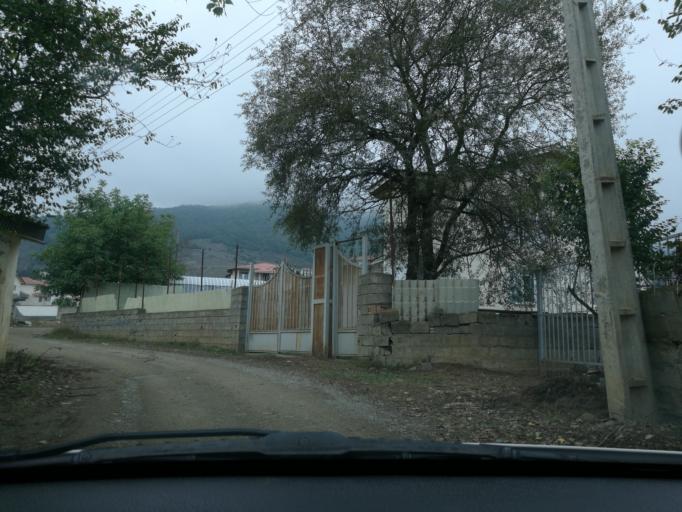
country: IR
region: Mazandaran
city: `Abbasabad
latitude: 36.5061
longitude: 51.1985
